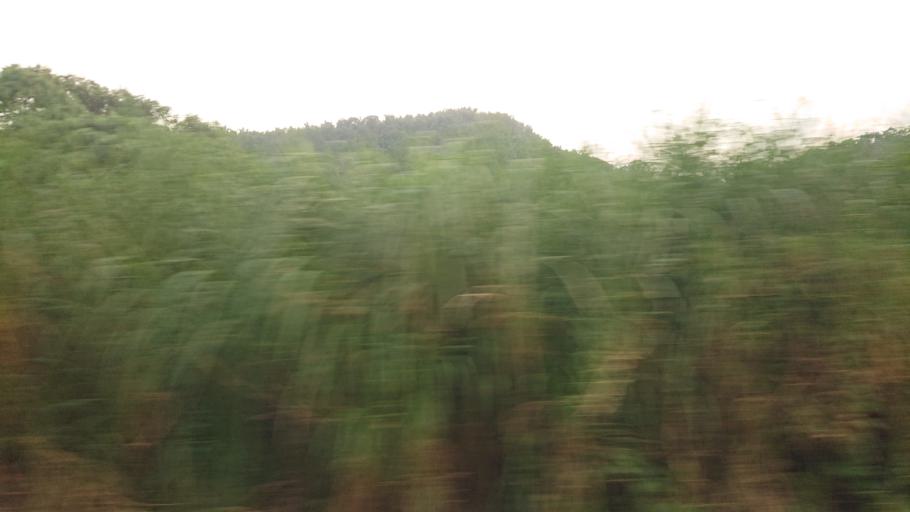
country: TW
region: Taiwan
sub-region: Nantou
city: Puli
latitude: 23.9739
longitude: 120.9919
